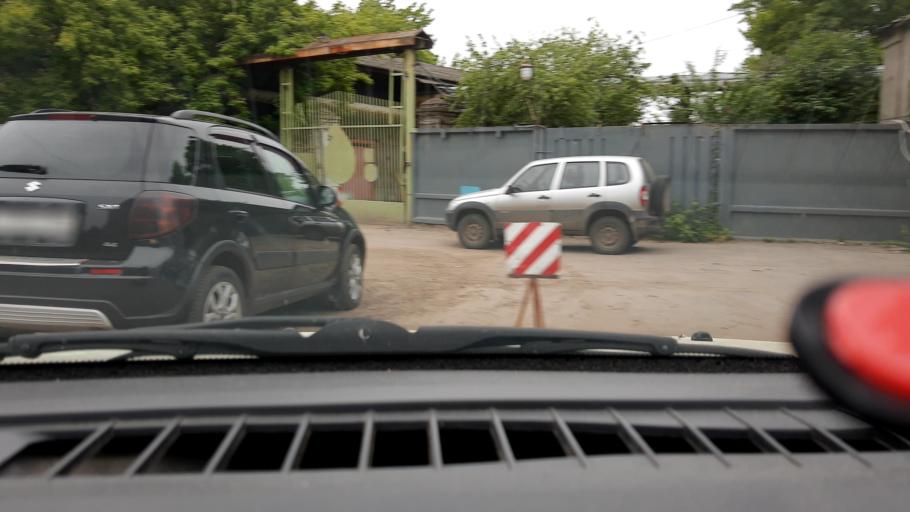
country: RU
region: Nizjnij Novgorod
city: Nizhniy Novgorod
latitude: 56.3192
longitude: 43.9180
